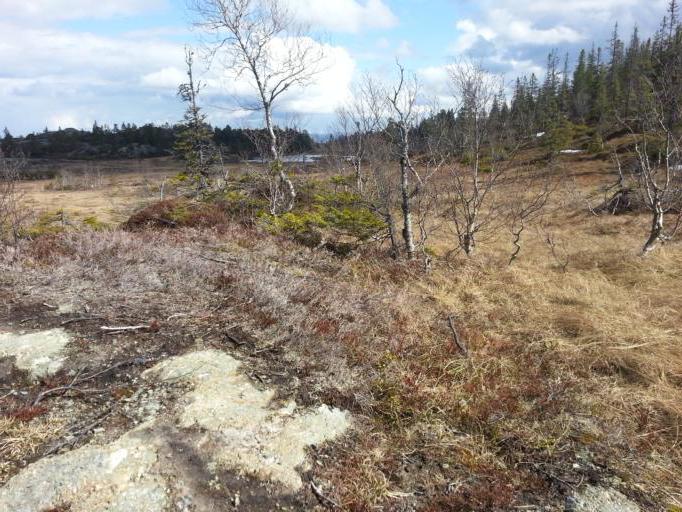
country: NO
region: Nord-Trondelag
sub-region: Levanger
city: Skogn
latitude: 63.5902
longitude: 11.0789
